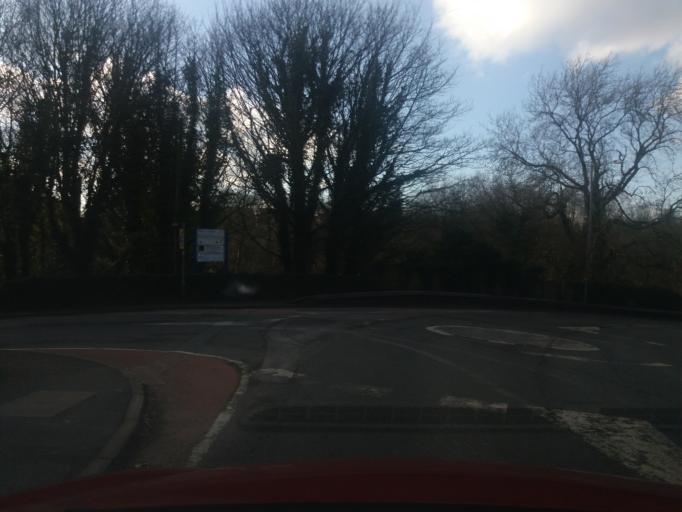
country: GB
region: England
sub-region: Lancashire
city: Chorley
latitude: 53.6465
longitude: -2.6121
